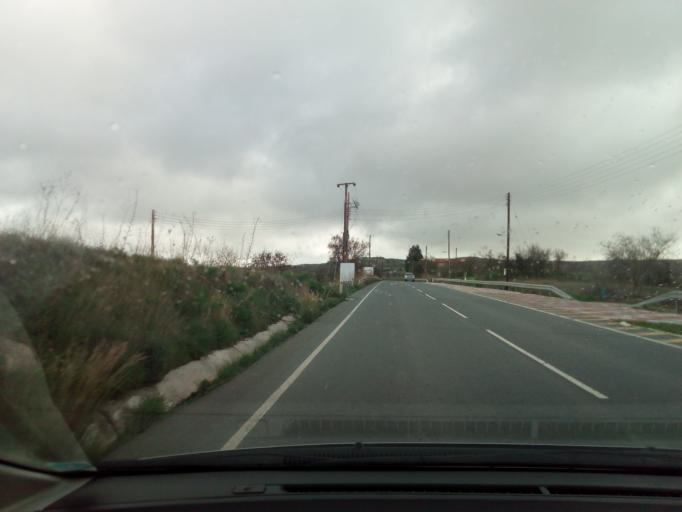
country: CY
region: Pafos
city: Tala
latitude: 34.9141
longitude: 32.4679
